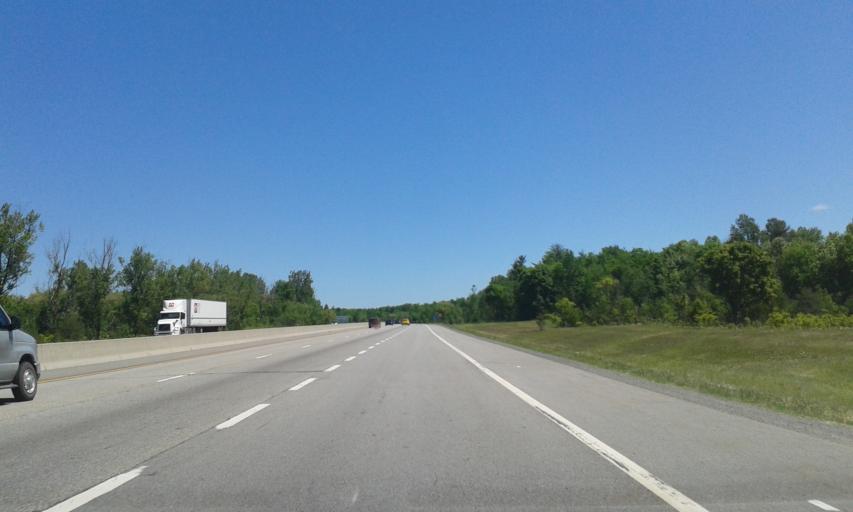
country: CA
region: Ontario
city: Prescott
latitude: 44.7575
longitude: -75.4735
